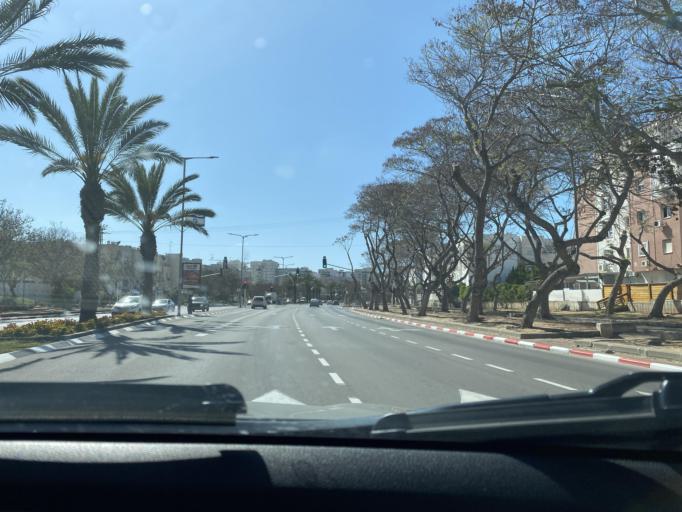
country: IL
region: Southern District
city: Ashqelon
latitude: 31.6737
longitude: 34.5829
